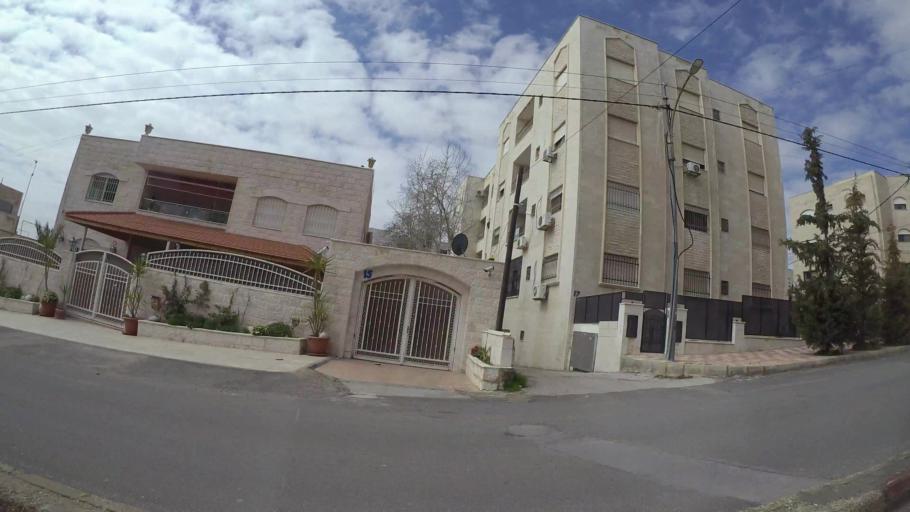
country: JO
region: Amman
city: Amman
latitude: 31.9985
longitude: 35.9143
